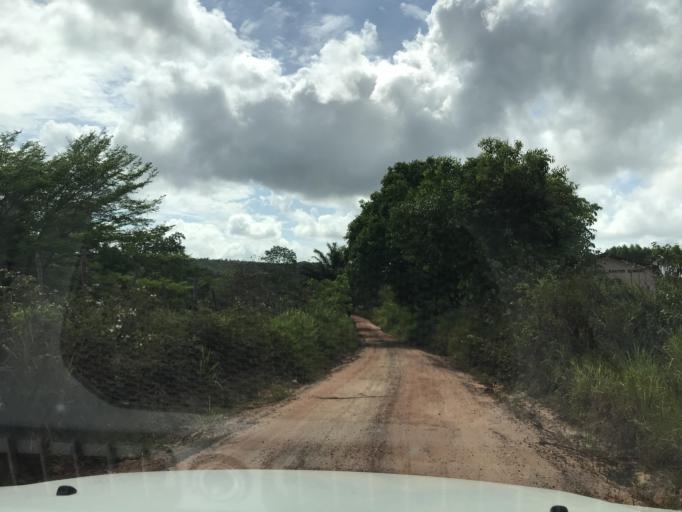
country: BR
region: Bahia
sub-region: Entre Rios
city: Entre Rios
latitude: -12.1778
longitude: -38.1265
